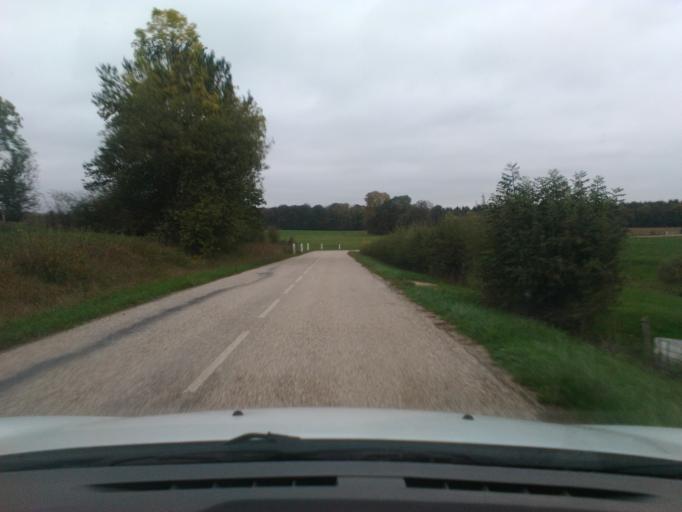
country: FR
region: Lorraine
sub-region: Departement des Vosges
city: Chavelot
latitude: 48.2830
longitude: 6.4641
